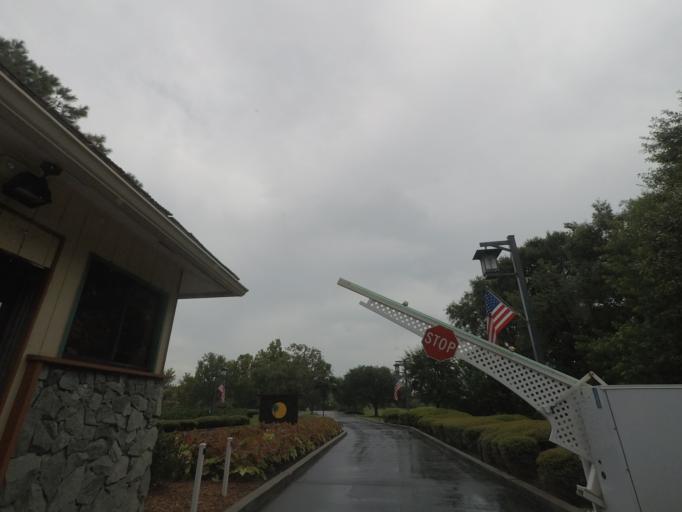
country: US
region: Florida
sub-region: Polk County
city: Citrus Ridge
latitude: 28.4038
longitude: -81.5887
